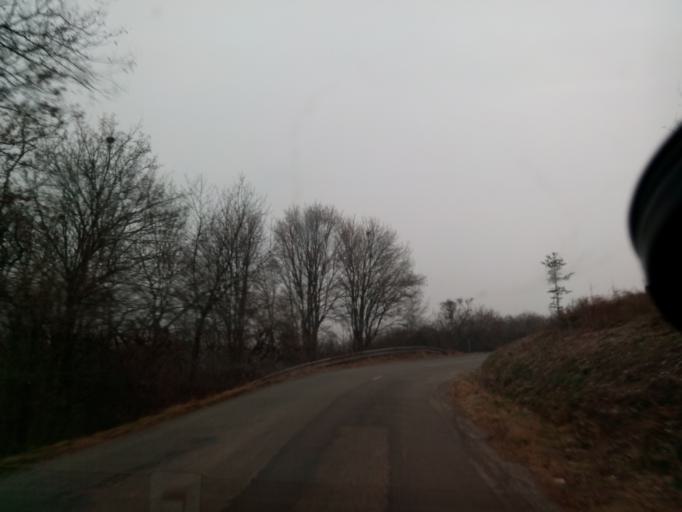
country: SK
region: Kosicky
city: Kosice
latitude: 48.7095
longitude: 21.1540
